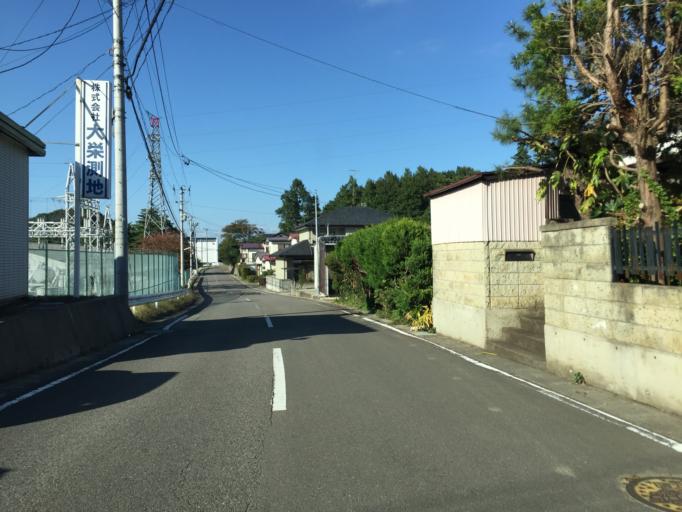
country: JP
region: Fukushima
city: Nihommatsu
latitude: 37.6564
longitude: 140.4865
